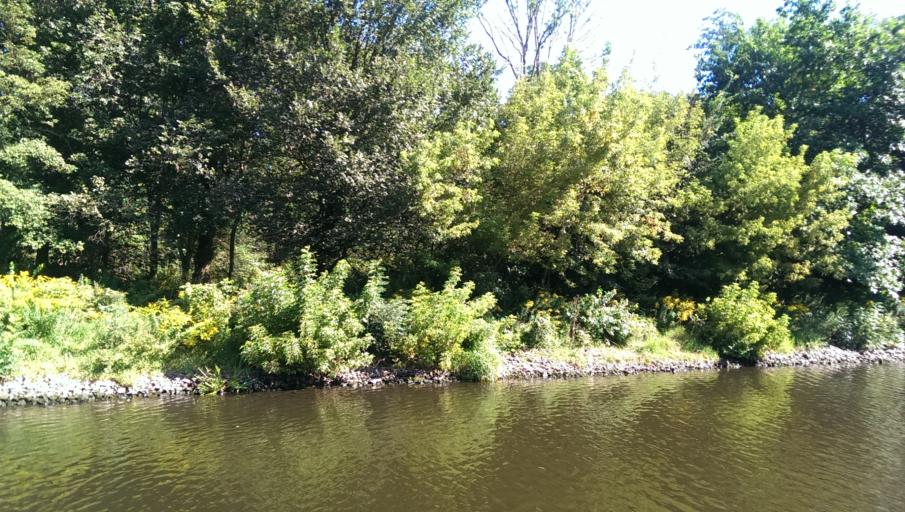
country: DE
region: Brandenburg
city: Stahnsdorf
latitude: 52.3982
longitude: 13.1914
